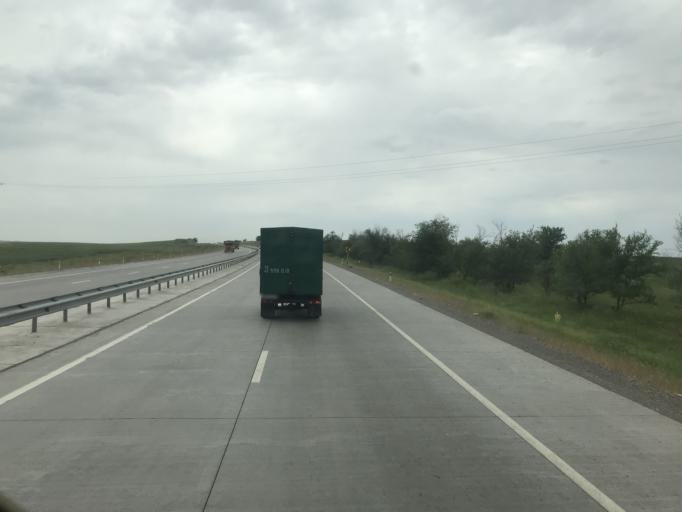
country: KZ
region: Ongtustik Qazaqstan
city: Shymkent
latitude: 42.2048
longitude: 69.5119
